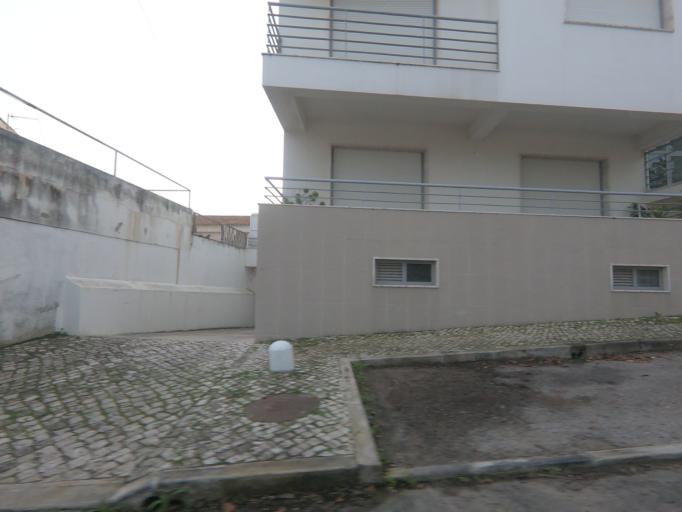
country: PT
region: Setubal
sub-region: Setubal
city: Setubal
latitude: 38.5244
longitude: -8.8539
